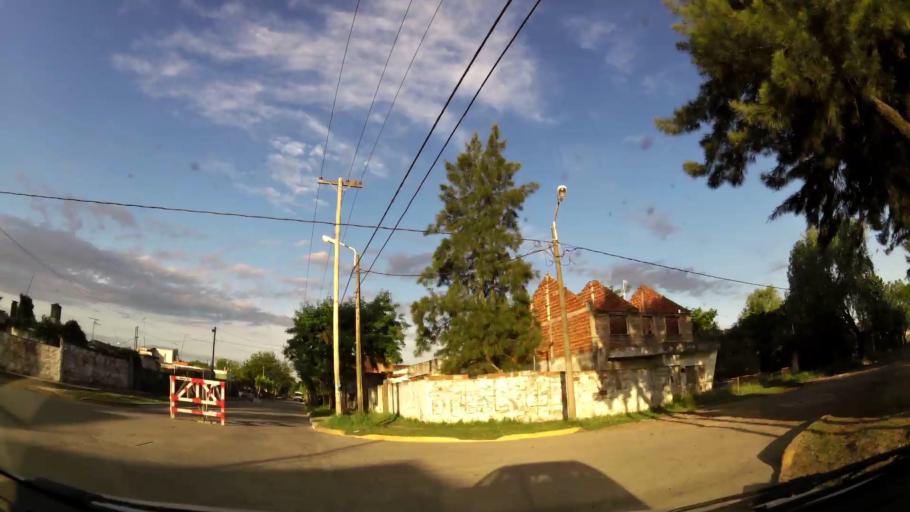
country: AR
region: Buenos Aires
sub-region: Partido de Merlo
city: Merlo
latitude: -34.6796
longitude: -58.7529
